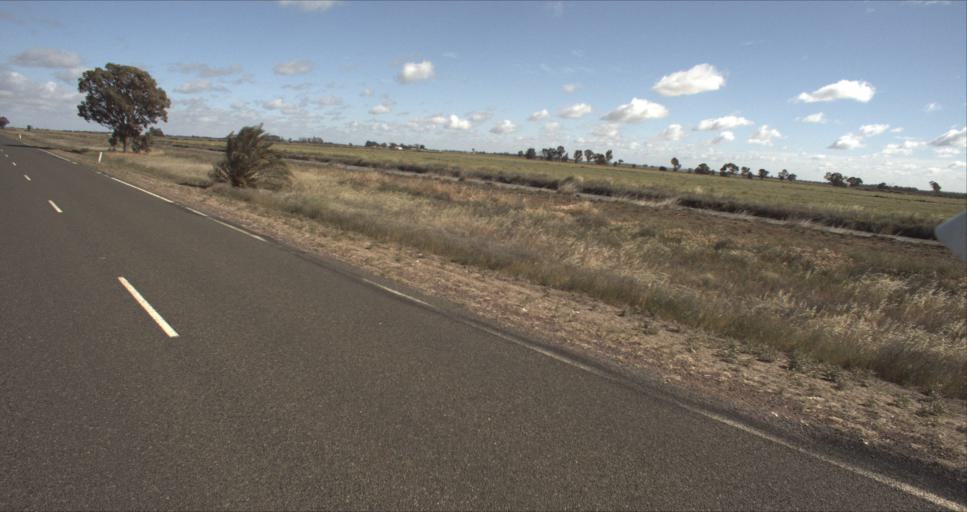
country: AU
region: New South Wales
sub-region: Leeton
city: Leeton
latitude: -34.5483
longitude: 146.2645
